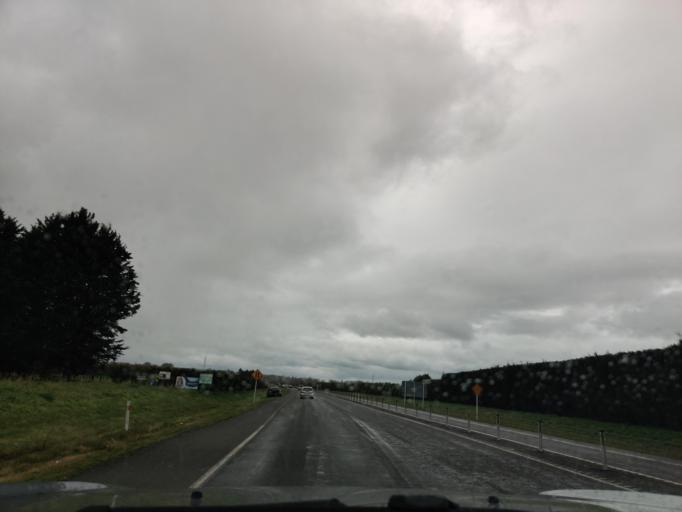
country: NZ
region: Hawke's Bay
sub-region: Hastings District
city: Hastings
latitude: -39.6057
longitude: 176.8390
